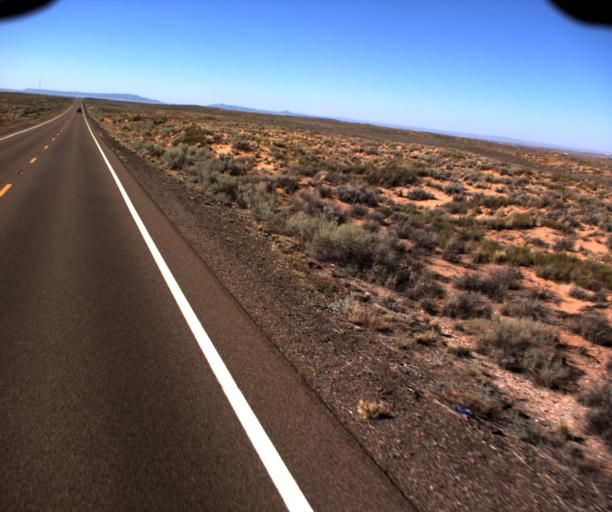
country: US
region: Arizona
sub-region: Navajo County
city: Winslow
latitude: 35.0480
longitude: -110.6003
